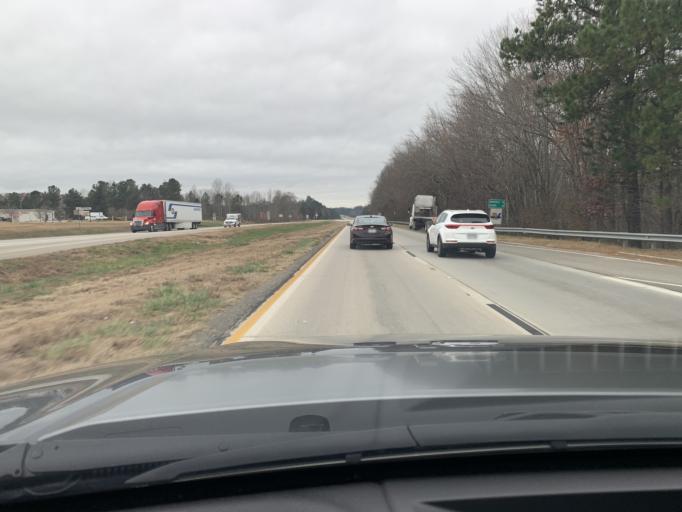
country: US
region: Georgia
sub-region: Hall County
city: Lula
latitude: 34.3946
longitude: -83.6924
